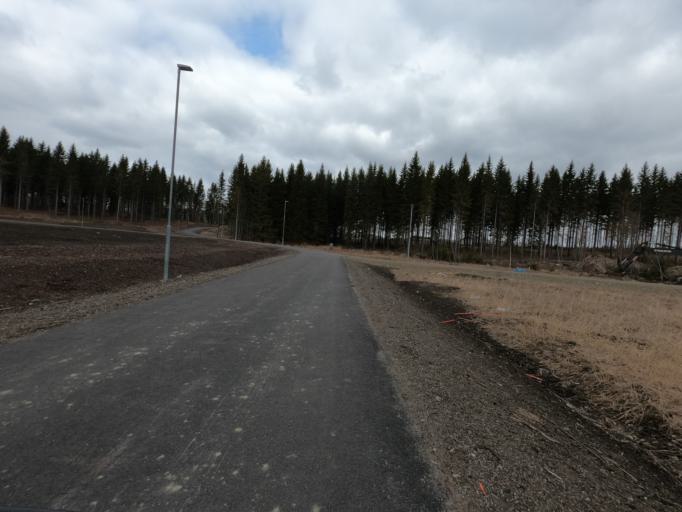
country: FI
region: North Karelia
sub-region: Joensuu
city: Joensuu
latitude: 62.5597
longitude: 29.8236
